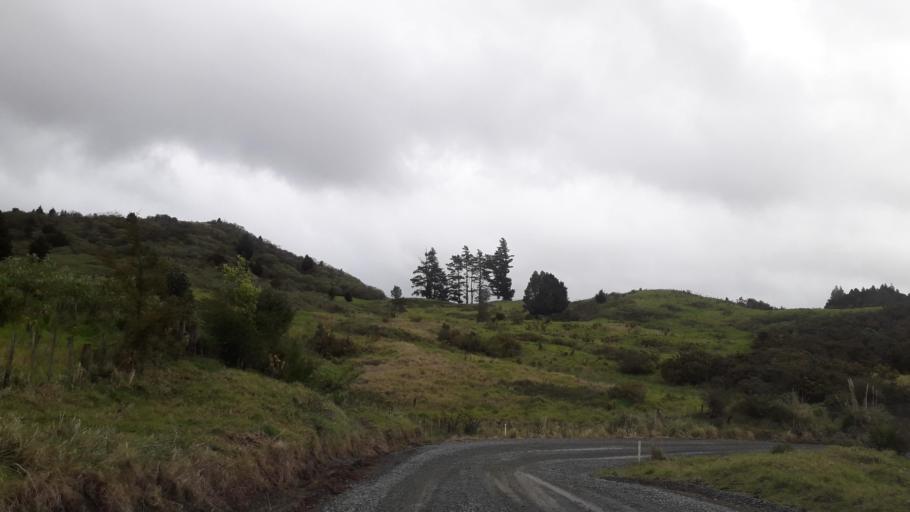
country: NZ
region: Northland
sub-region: Far North District
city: Kerikeri
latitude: -35.1325
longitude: 173.7356
